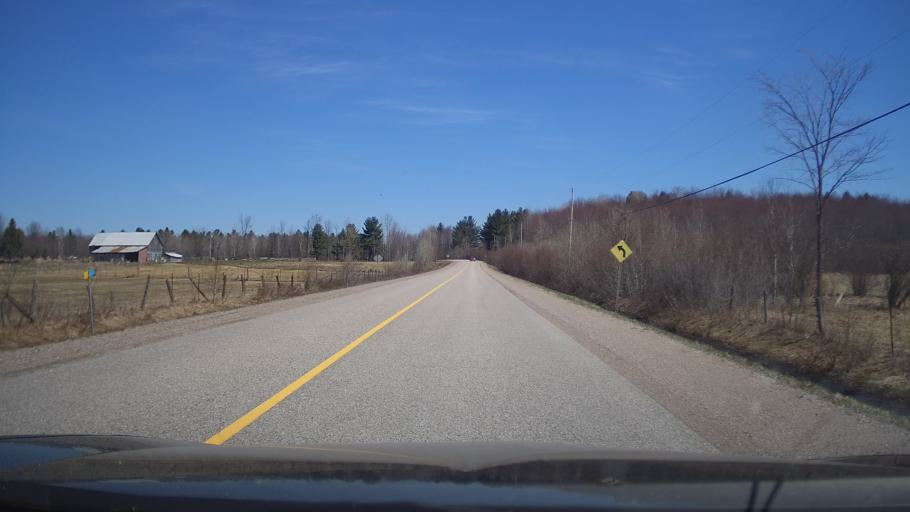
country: CA
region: Ontario
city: Arnprior
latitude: 45.5403
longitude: -76.3671
